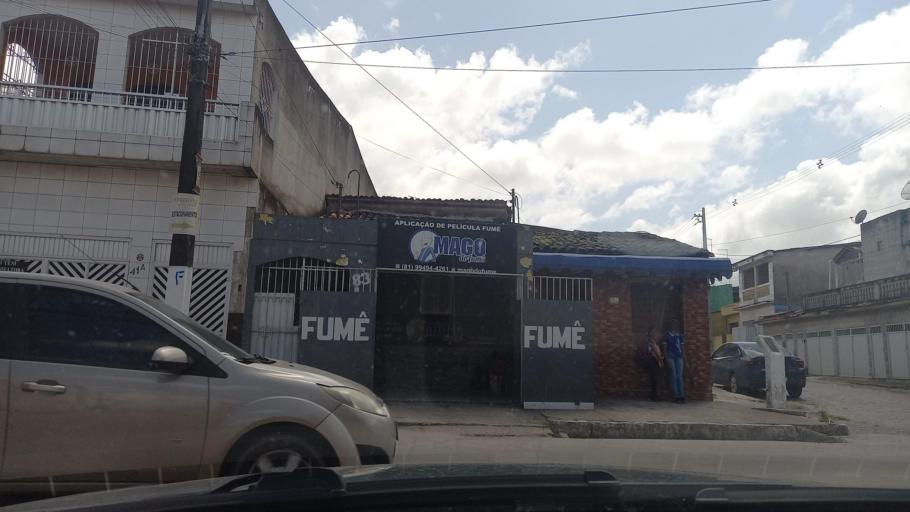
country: BR
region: Pernambuco
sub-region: Goiana
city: Goiana
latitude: -7.5643
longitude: -35.0081
